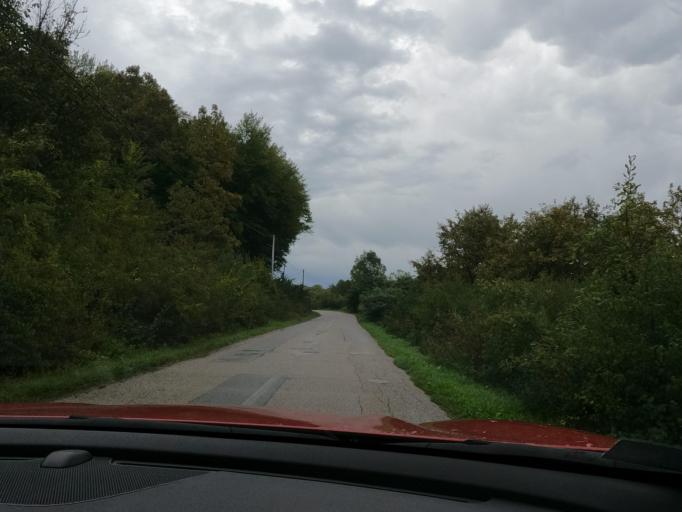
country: HR
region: Sisacko-Moslavacka
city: Glina
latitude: 45.2956
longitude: 16.1508
